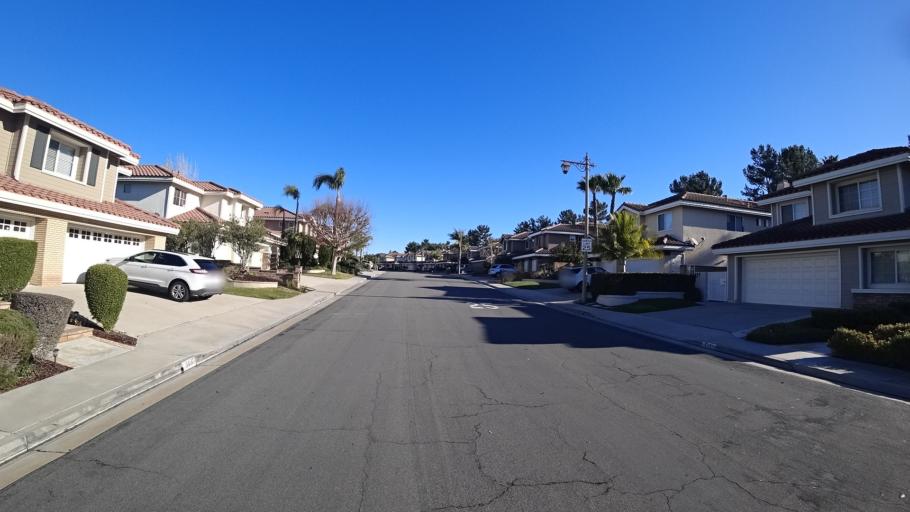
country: US
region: California
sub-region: Orange County
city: Yorba Linda
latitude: 33.8633
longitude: -117.7323
